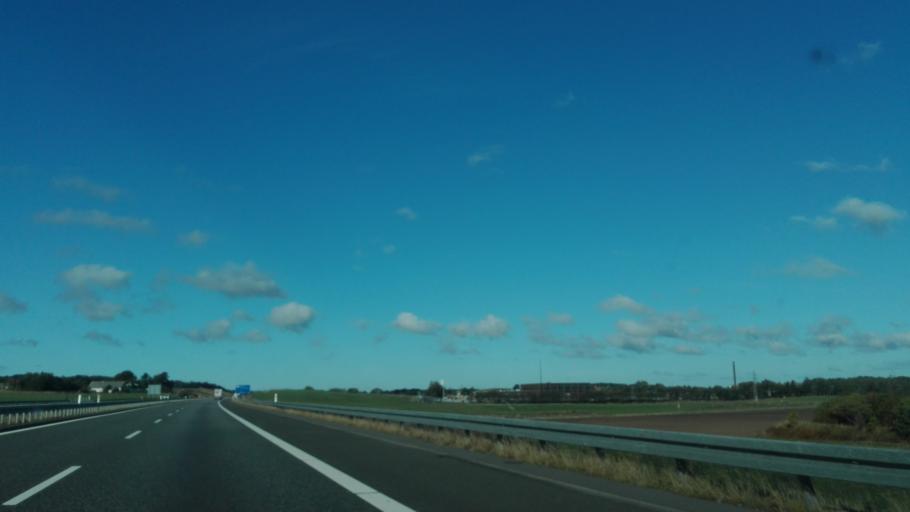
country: DK
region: Central Jutland
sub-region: Silkeborg Kommune
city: Svejbaek
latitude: 56.1485
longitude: 9.6604
